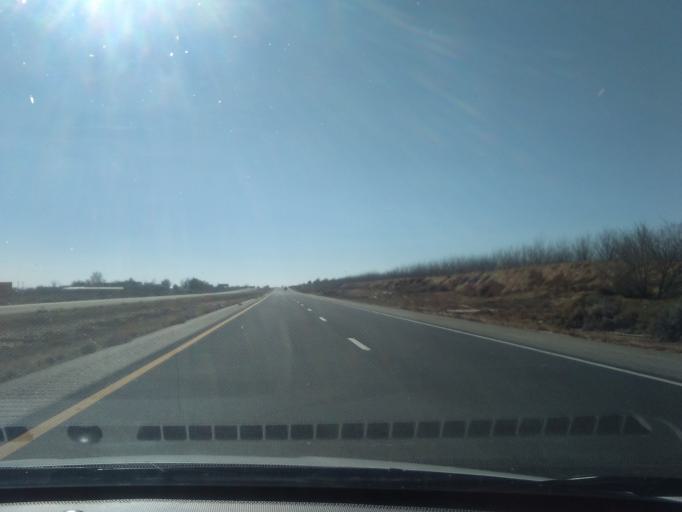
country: US
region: New Mexico
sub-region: Valencia County
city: Jarales
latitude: 34.6042
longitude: -106.7872
